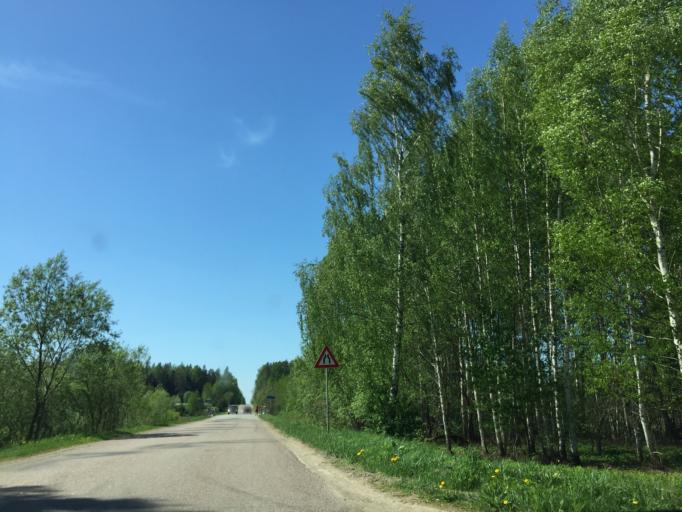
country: LV
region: Ogre
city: Ogre
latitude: 56.8561
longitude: 24.6973
